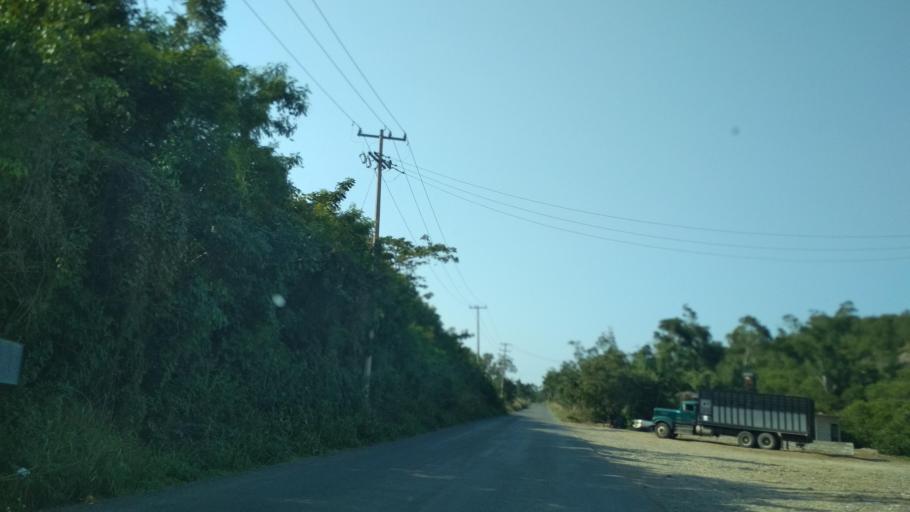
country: MX
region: Veracruz
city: Agua Dulce
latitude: 20.3961
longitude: -97.2120
